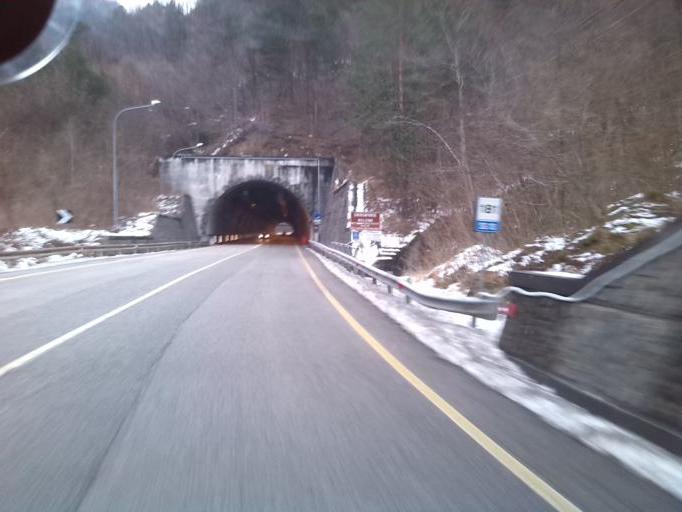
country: IT
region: Friuli Venezia Giulia
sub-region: Provincia di Udine
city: Chiusaforte
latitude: 46.3951
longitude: 13.2629
